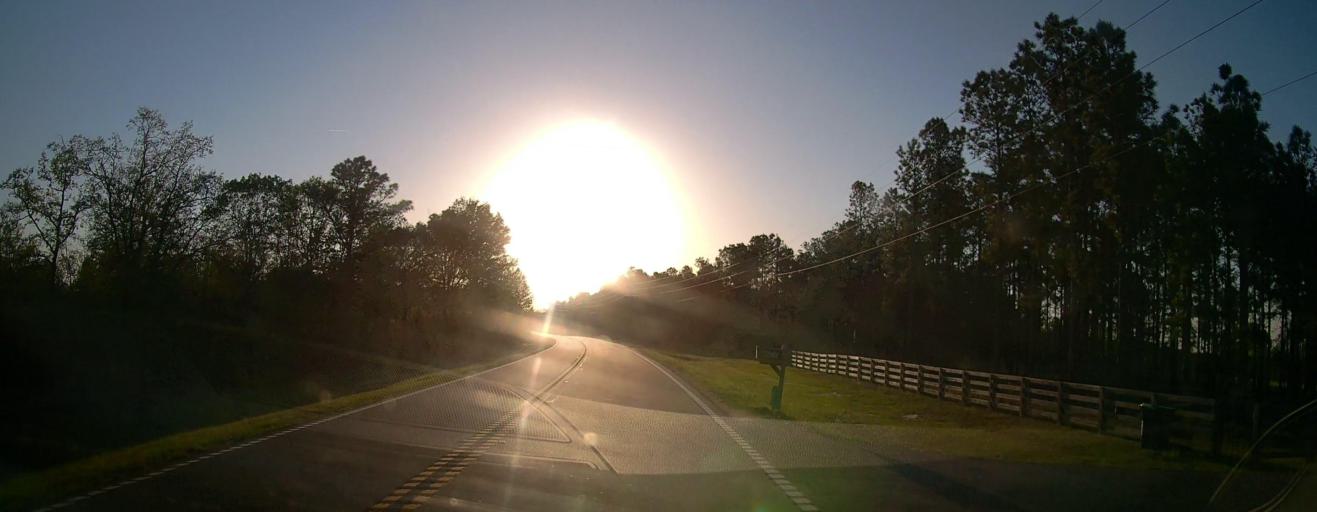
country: US
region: Georgia
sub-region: Talbot County
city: Talbotton
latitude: 32.5367
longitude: -84.5010
